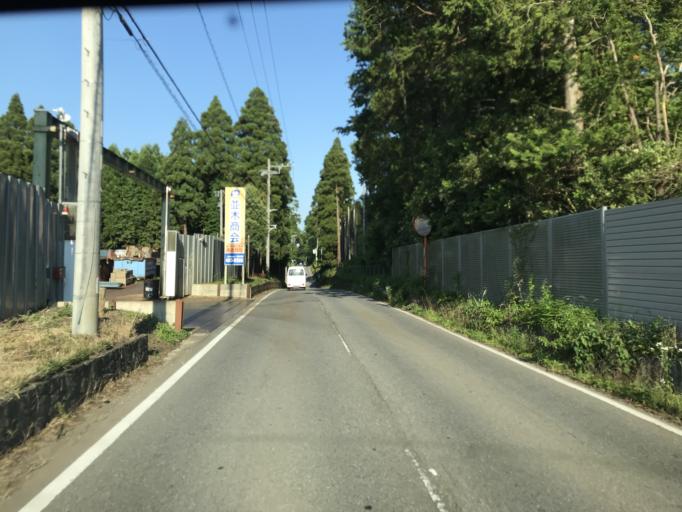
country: JP
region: Chiba
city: Yachimata
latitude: 35.6010
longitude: 140.2540
